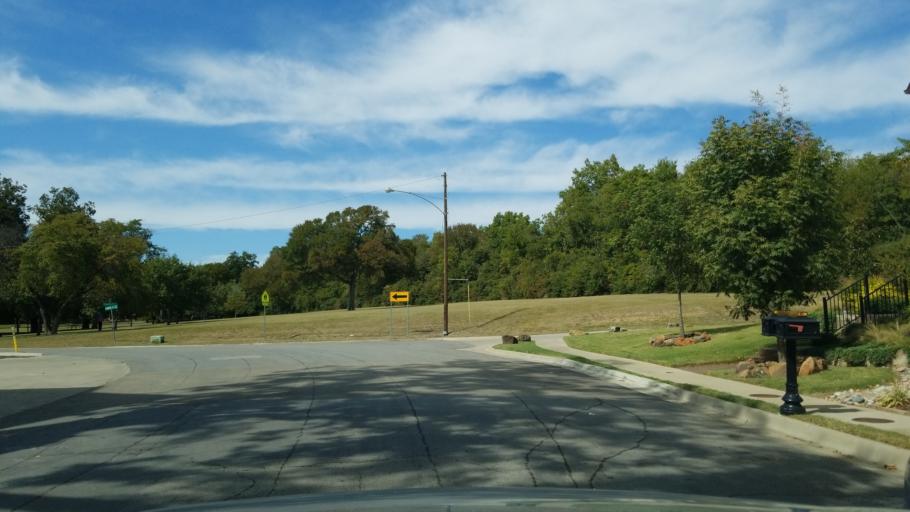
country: US
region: Texas
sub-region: Dallas County
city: Highland Park
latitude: 32.8087
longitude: -96.7365
